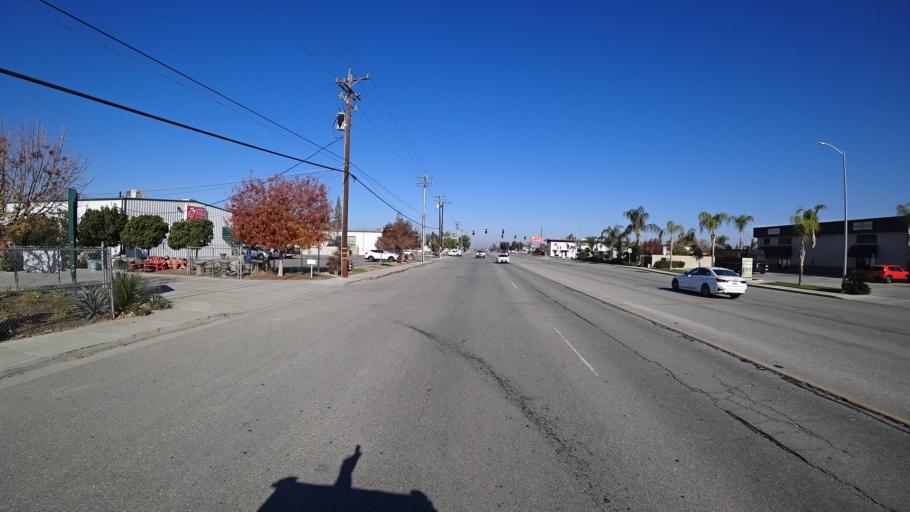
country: US
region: California
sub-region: Kern County
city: Rosedale
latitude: 35.3898
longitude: -119.1456
